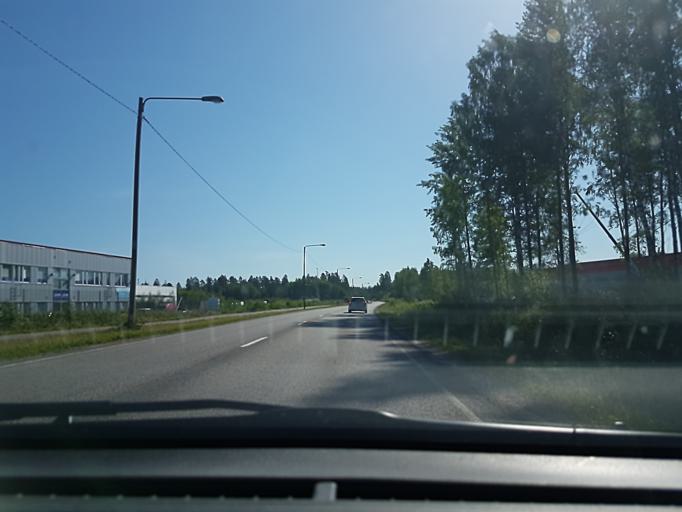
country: FI
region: Uusimaa
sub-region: Helsinki
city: Vantaa
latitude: 60.3440
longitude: 25.0268
